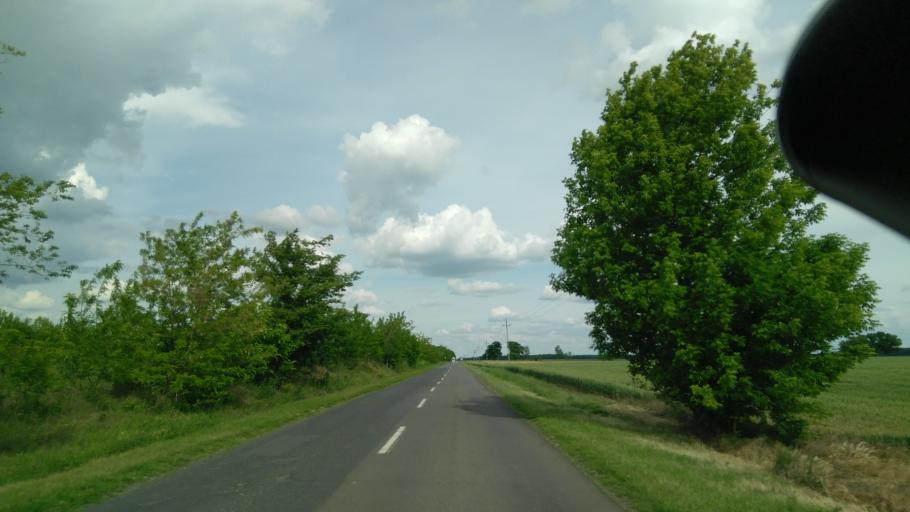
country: RO
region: Arad
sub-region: Comuna Peregu Mare
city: Peregu Mare
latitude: 46.3056
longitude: 20.8988
